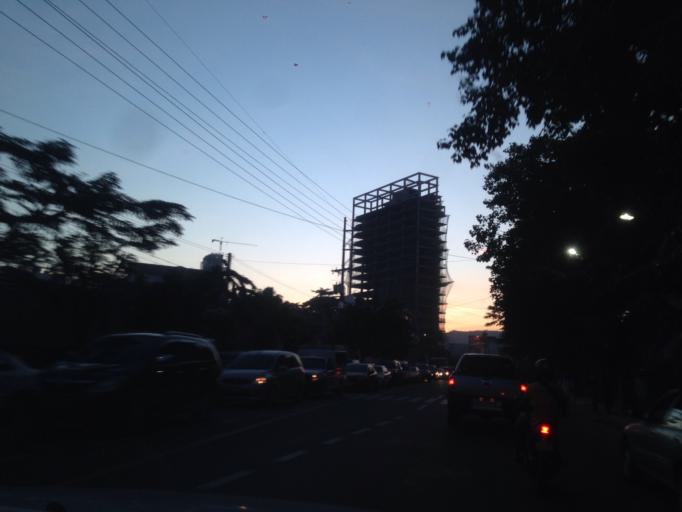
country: PH
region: Central Visayas
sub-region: Cebu City
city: Baugo
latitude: 10.3093
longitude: 123.9062
